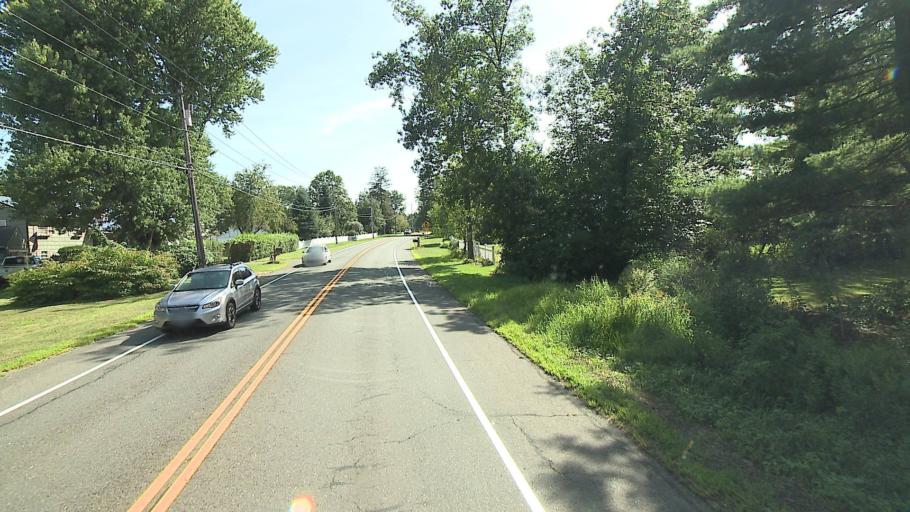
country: US
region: Connecticut
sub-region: Hartford County
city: Weatogue
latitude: 41.8524
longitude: -72.8341
